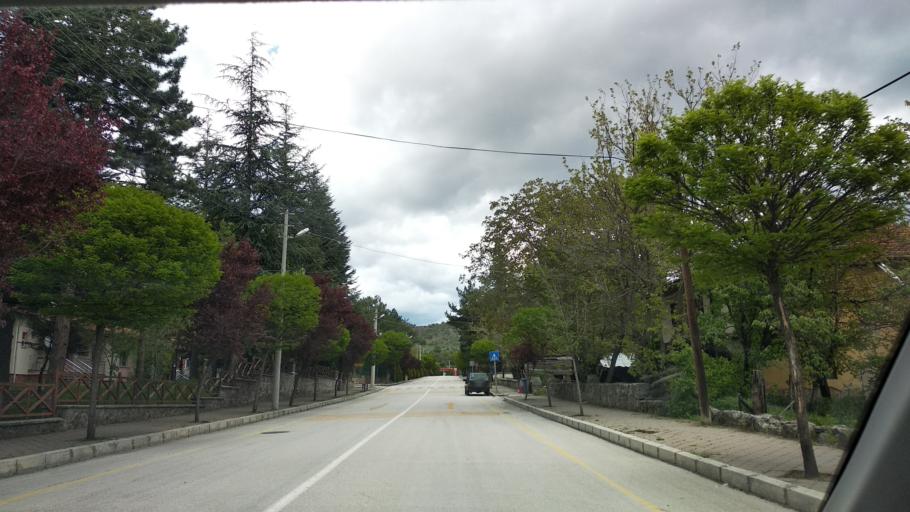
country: TR
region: Bolu
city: Seben
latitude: 40.4130
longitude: 31.5743
